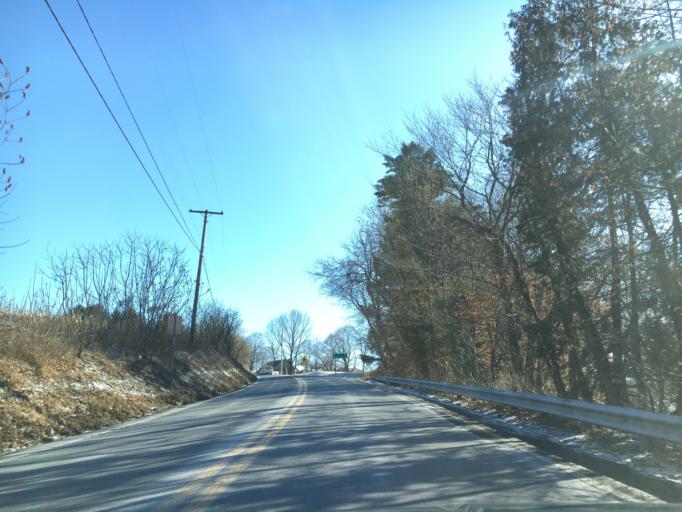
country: US
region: Pennsylvania
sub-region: Lehigh County
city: Schnecksville
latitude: 40.6791
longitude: -75.5730
